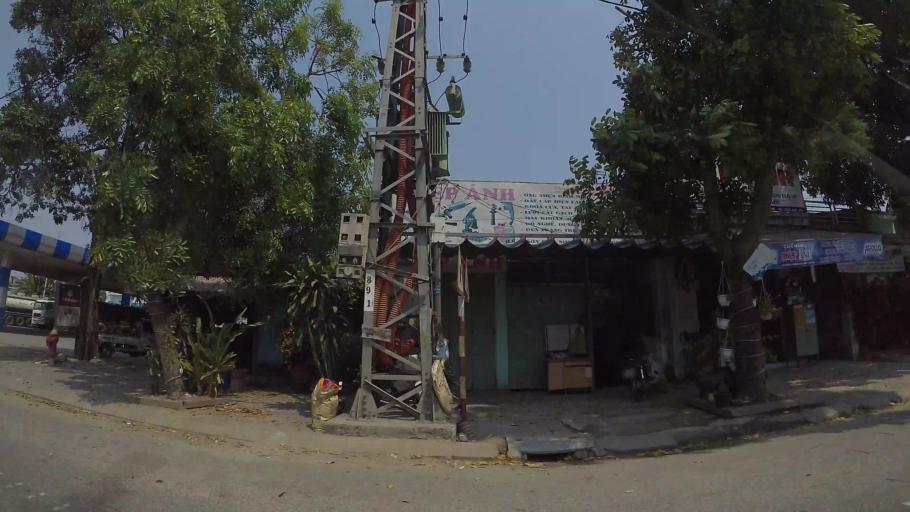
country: VN
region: Da Nang
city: Cam Le
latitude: 15.9777
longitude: 108.2084
